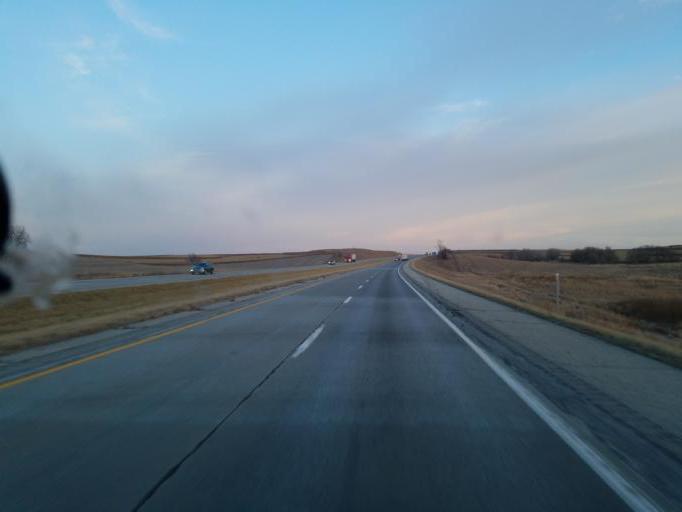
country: US
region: Iowa
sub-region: Pottawattamie County
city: Avoca
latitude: 41.5002
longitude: -95.5230
